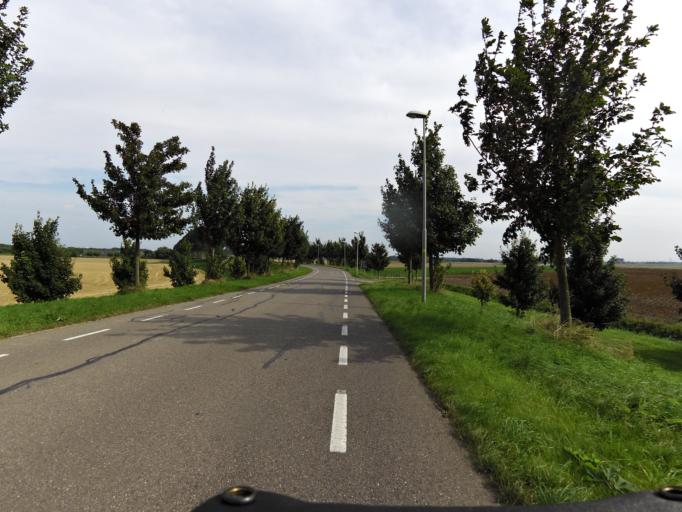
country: NL
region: South Holland
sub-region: Gemeente Zwijndrecht
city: Heerjansdam
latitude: 51.7927
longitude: 4.5876
